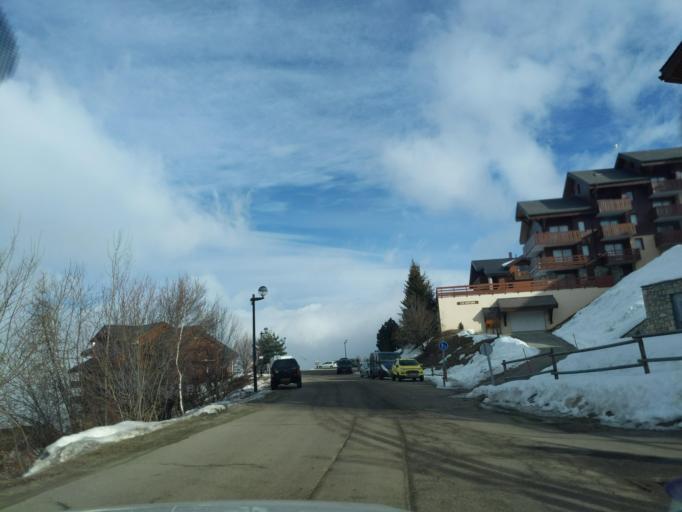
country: FR
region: Rhone-Alpes
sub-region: Departement de la Savoie
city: Bourg-Saint-Maurice
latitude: 45.5575
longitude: 6.7623
